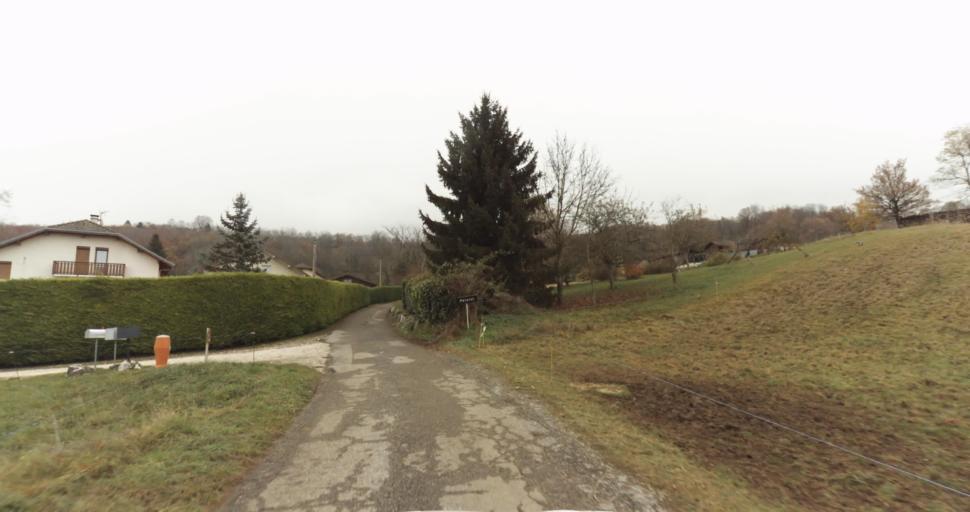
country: FR
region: Rhone-Alpes
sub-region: Departement de la Haute-Savoie
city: Cusy
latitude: 45.7524
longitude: 6.0143
